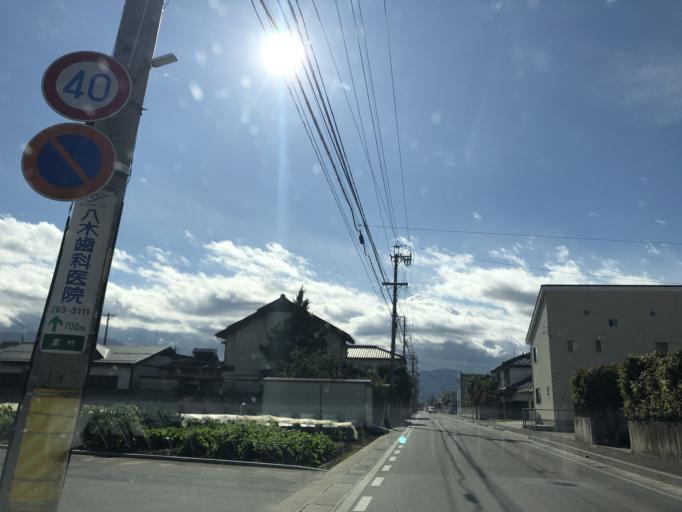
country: JP
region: Nagano
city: Suzaka
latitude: 36.6689
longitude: 138.2577
